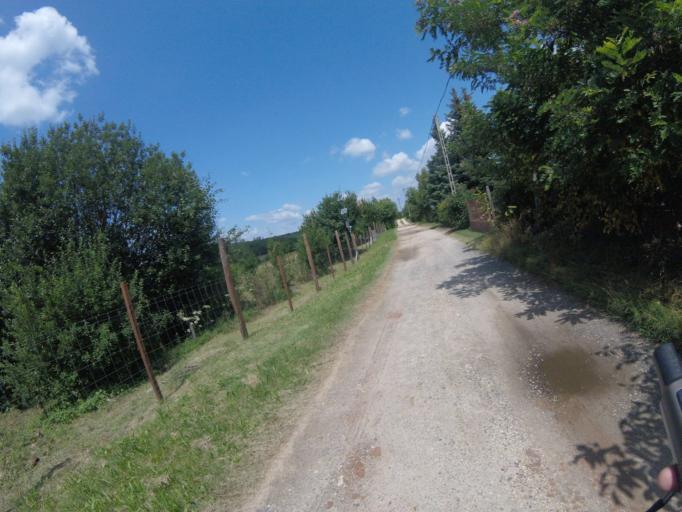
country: HU
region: Zala
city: Nagykanizsa
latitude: 46.5537
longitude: 17.0344
